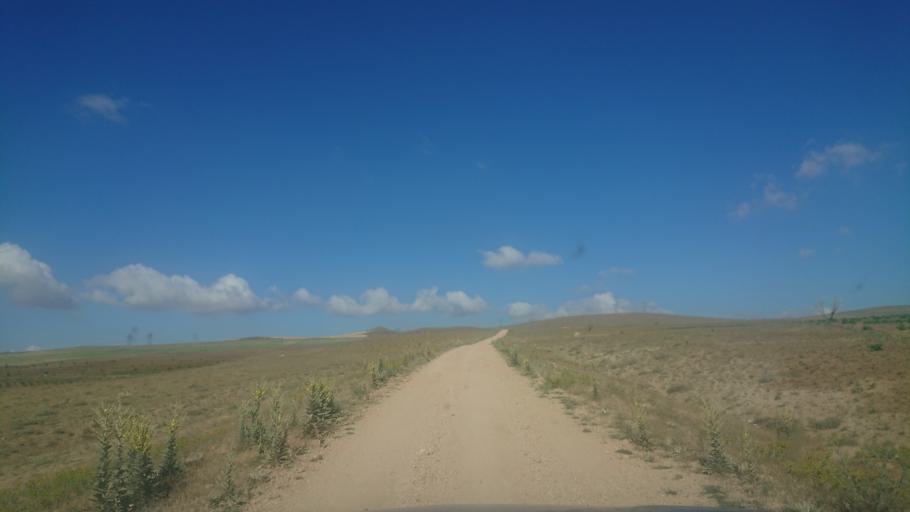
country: TR
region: Aksaray
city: Agacoren
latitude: 38.9175
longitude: 33.9158
